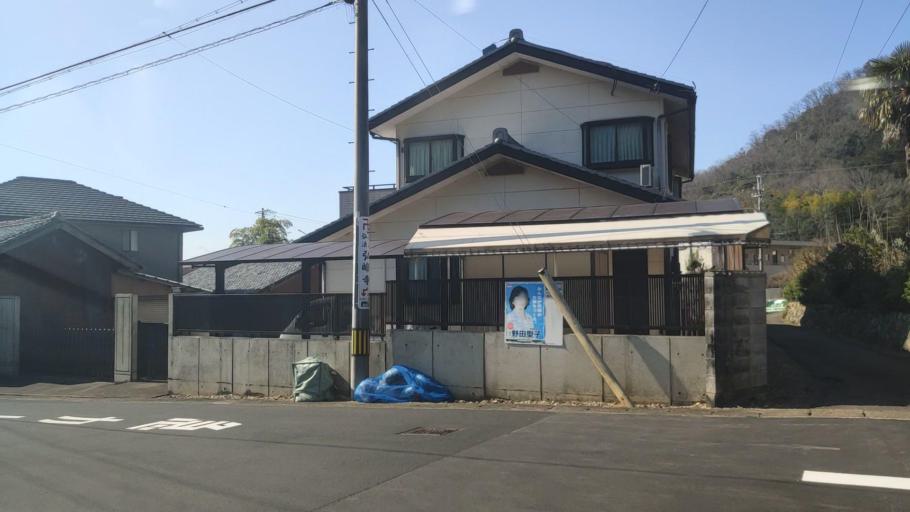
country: JP
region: Gifu
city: Gifu-shi
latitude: 35.4236
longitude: 136.7848
